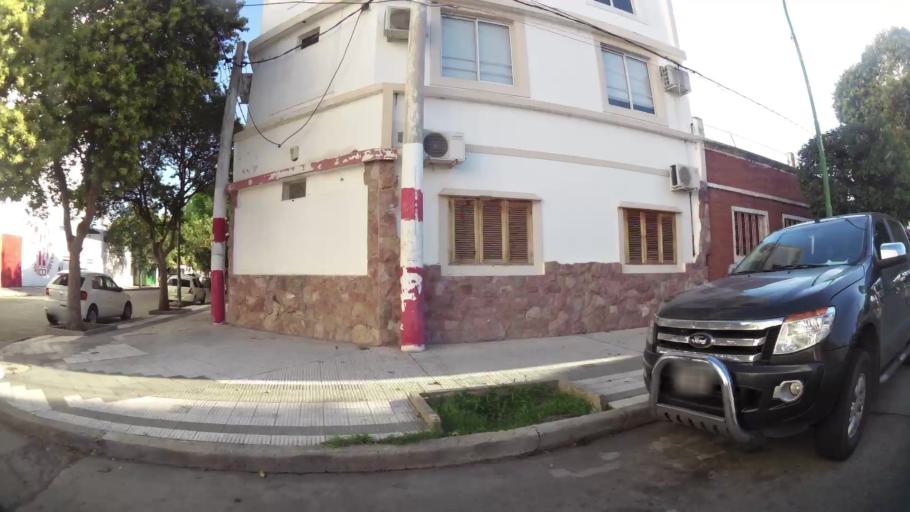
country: AR
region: Cordoba
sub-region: Departamento de Capital
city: Cordoba
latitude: -31.3841
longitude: -64.1812
